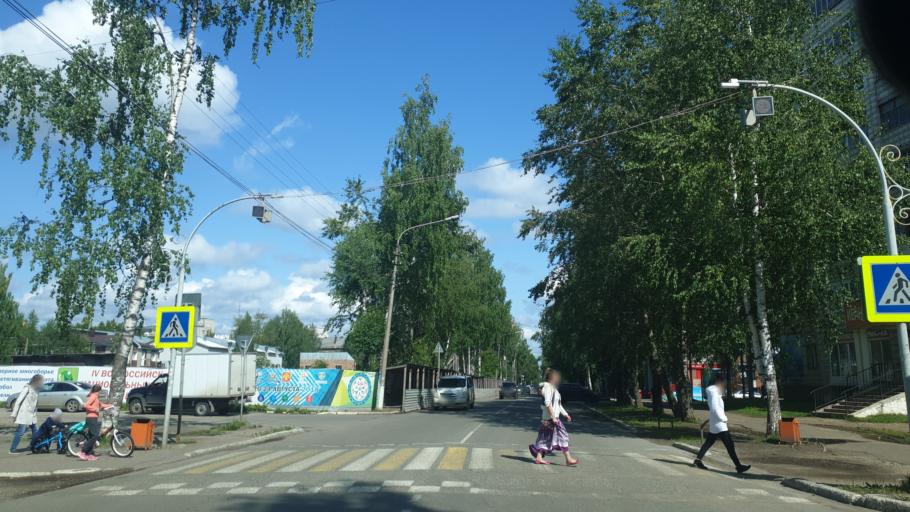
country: RU
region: Komi Republic
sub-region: Syktyvdinskiy Rayon
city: Syktyvkar
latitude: 61.6630
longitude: 50.8289
